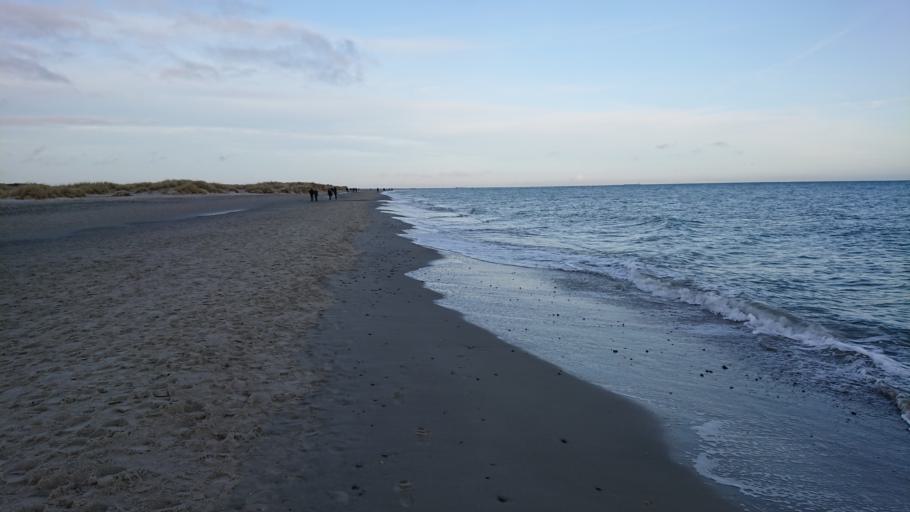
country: DK
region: North Denmark
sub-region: Frederikshavn Kommune
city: Skagen
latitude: 57.7420
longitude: 10.6428
